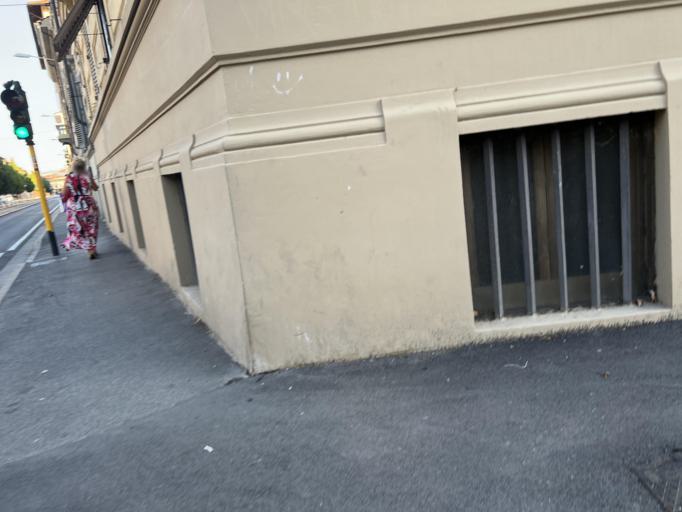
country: IT
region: Tuscany
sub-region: Province of Florence
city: Florence
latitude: 43.7908
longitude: 11.2475
